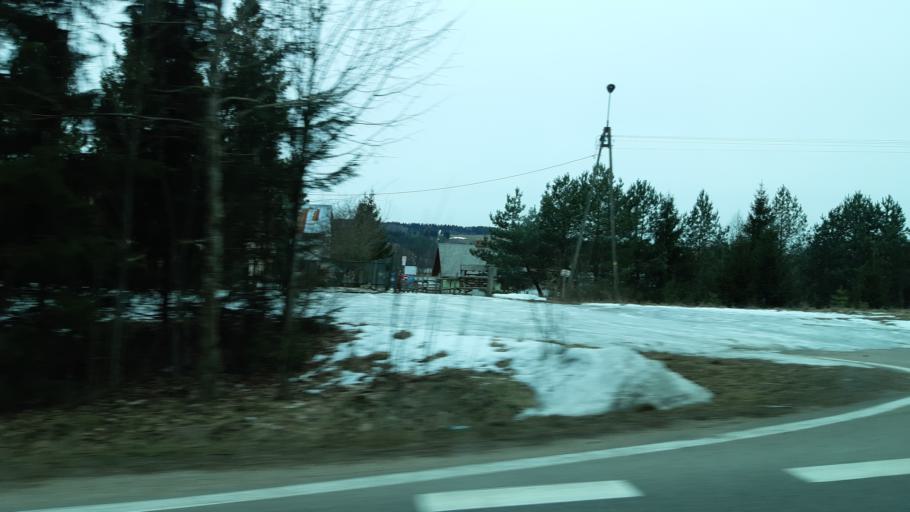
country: PL
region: Podlasie
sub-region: Suwalki
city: Suwalki
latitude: 54.3119
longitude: 22.9580
